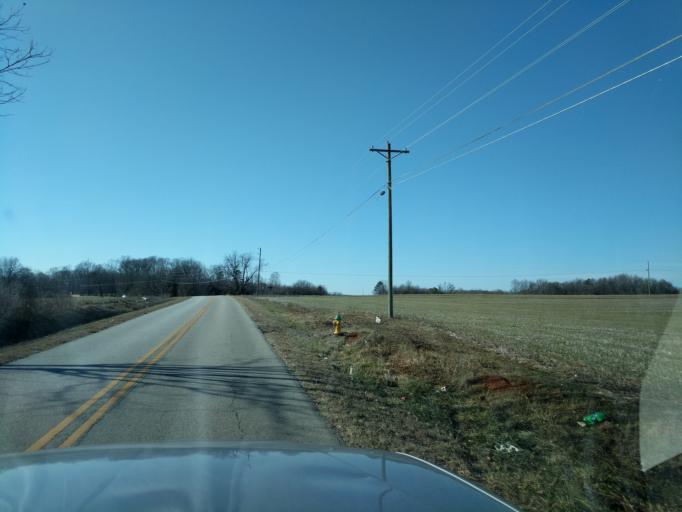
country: US
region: Georgia
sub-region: Hart County
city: Hartwell
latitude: 34.3294
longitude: -82.8800
